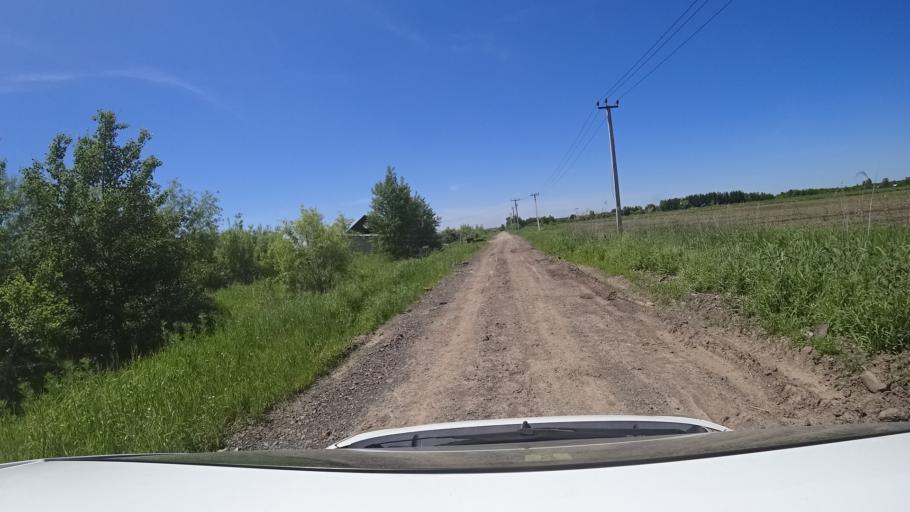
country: RU
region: Khabarovsk Krai
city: Topolevo
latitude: 48.4992
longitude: 135.2042
